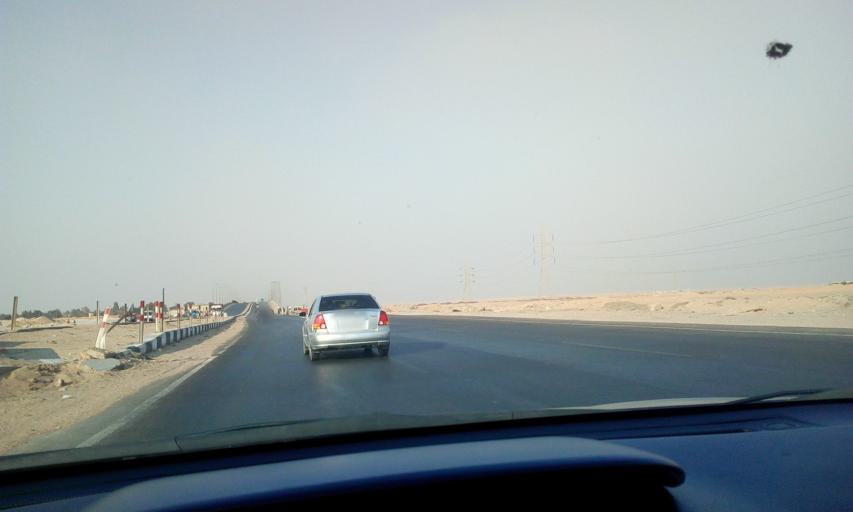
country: EG
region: Al Jizah
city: Madinat Sittah Uktubar
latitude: 29.8706
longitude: 31.0738
